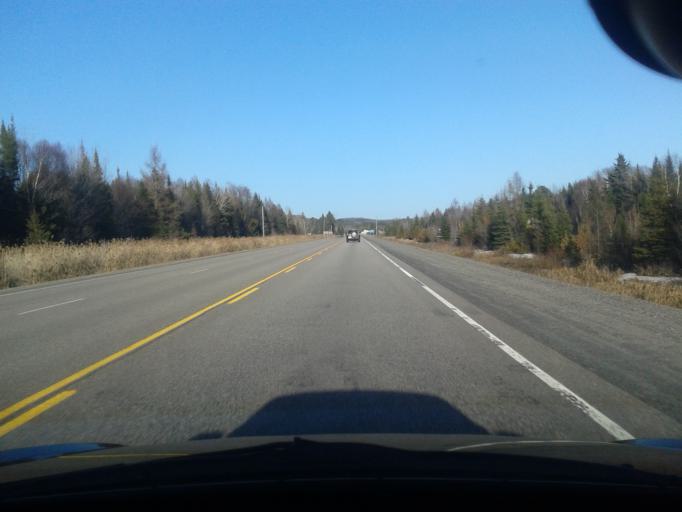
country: CA
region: Ontario
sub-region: Nipissing District
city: North Bay
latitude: 46.3700
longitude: -79.7199
